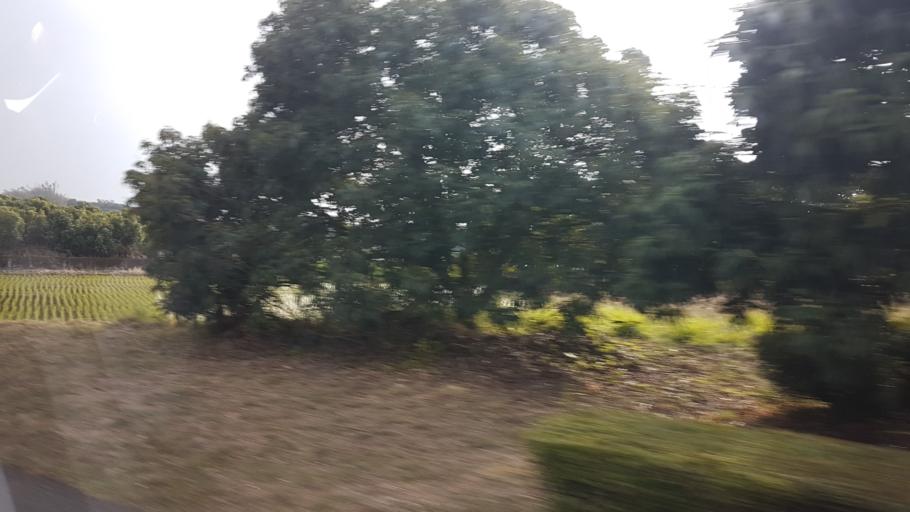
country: TW
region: Taiwan
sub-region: Chiayi
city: Jiayi Shi
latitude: 23.3890
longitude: 120.4345
